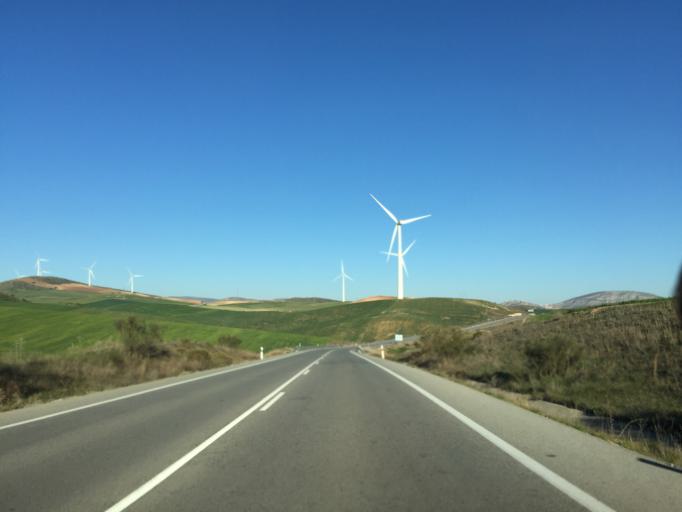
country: ES
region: Andalusia
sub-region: Provincia de Malaga
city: Ardales
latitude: 36.9312
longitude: -4.8575
